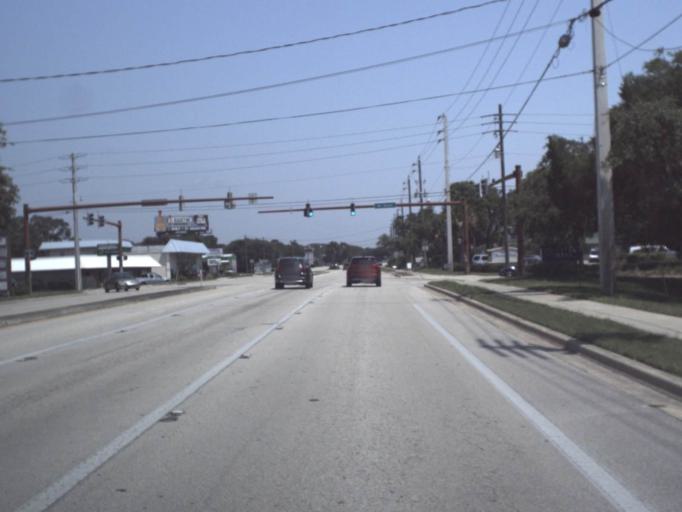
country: US
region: Florida
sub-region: Saint Johns County
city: Saint Augustine Beach
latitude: 29.8548
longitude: -81.2798
